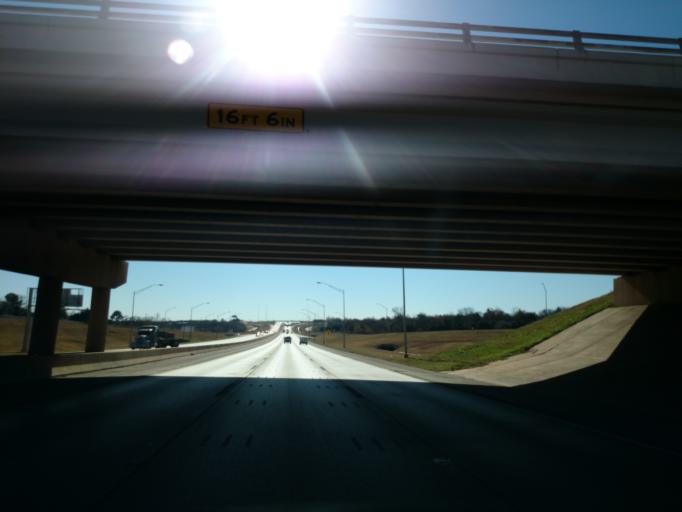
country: US
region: Oklahoma
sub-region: Oklahoma County
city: Edmond
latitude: 35.6238
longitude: -97.4250
